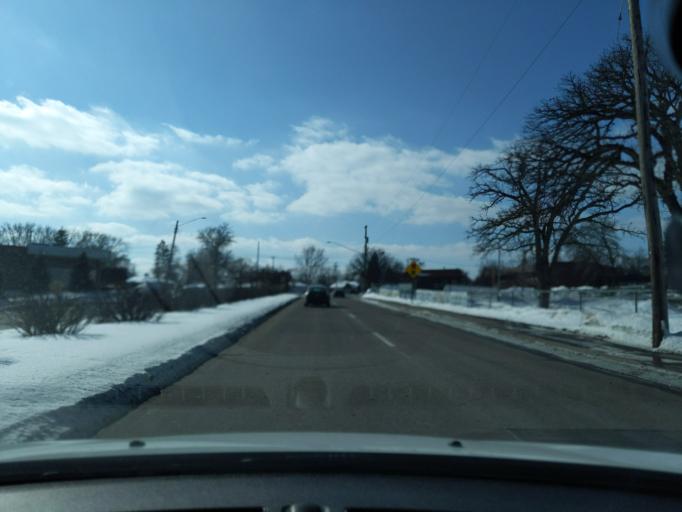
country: US
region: Minnesota
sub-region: Hennepin County
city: Saint Anthony
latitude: 45.0143
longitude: -93.2239
